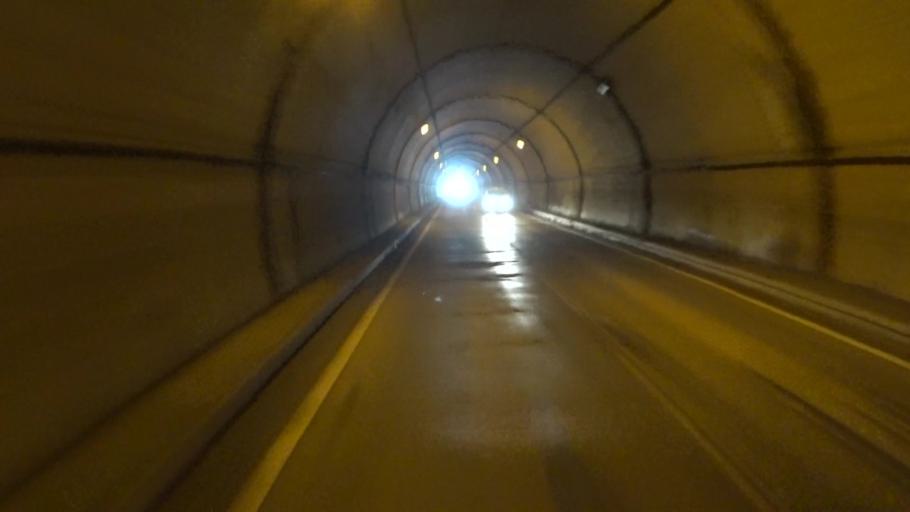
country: JP
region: Kyoto
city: Miyazu
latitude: 35.7517
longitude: 135.1376
